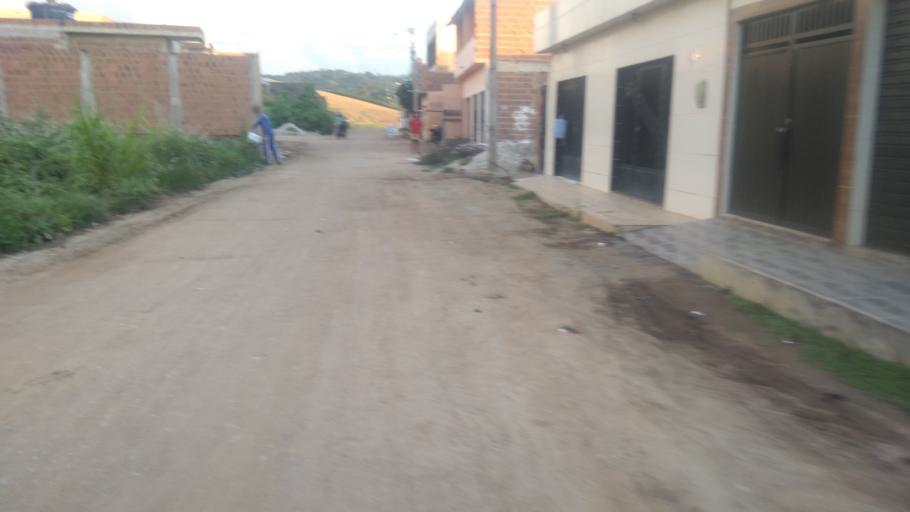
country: BR
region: Pernambuco
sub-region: Vitoria De Santo Antao
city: Vitoria de Santo Antao
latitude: -8.1248
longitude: -35.2800
